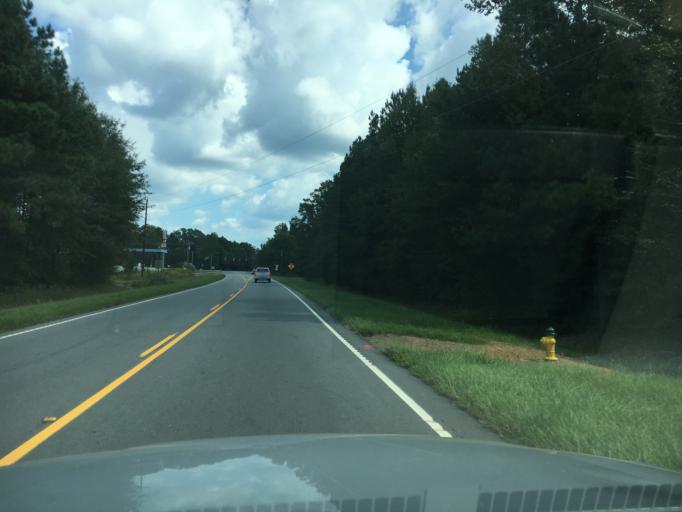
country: US
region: South Carolina
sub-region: Greenwood County
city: Greenwood
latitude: 34.1375
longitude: -82.1339
